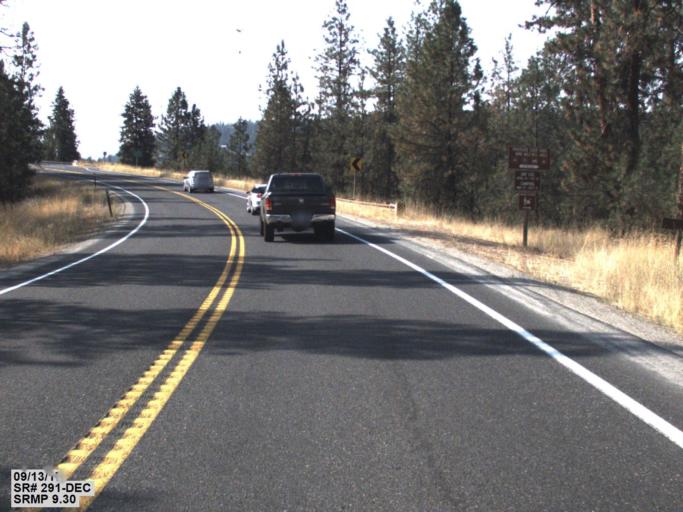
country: US
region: Washington
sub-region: Spokane County
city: Fairwood
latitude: 47.7784
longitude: -117.5439
